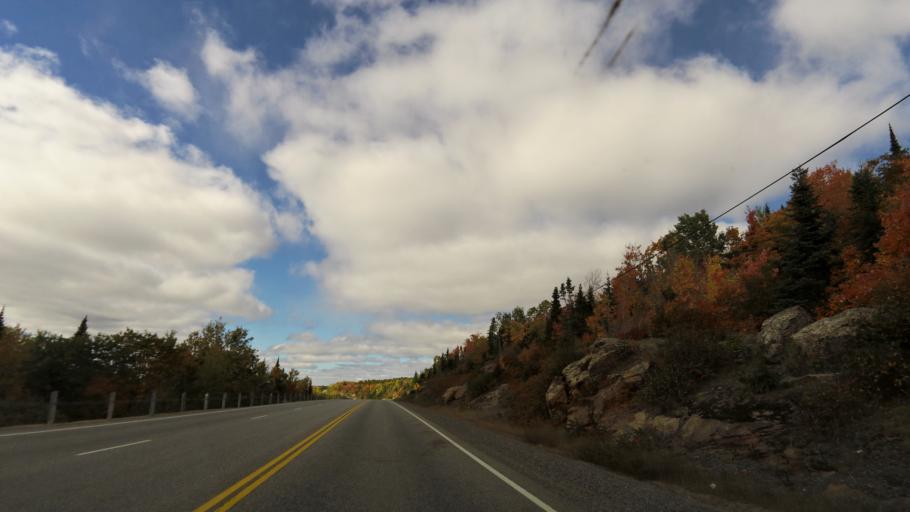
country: CA
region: Ontario
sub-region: Nipissing District
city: North Bay
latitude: 46.3617
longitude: -79.6648
